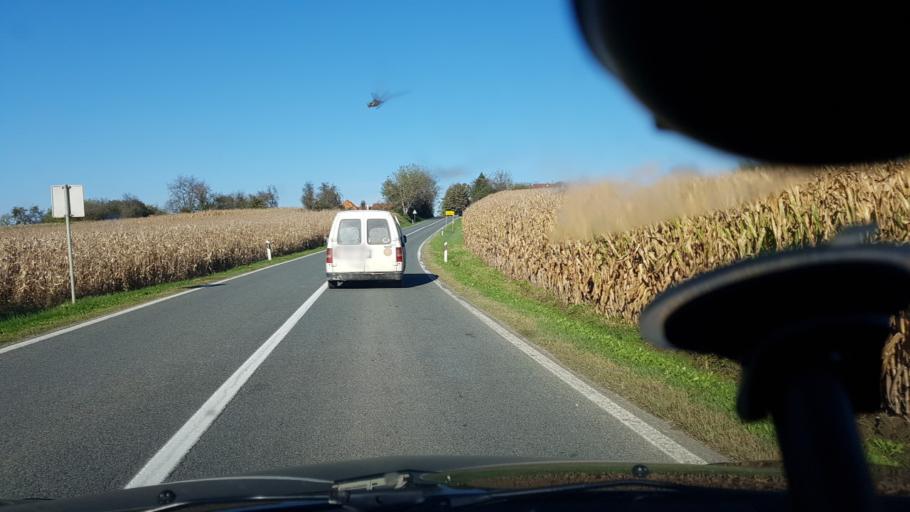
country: HR
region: Bjelovarsko-Bilogorska
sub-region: Grad Cazma
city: Cazma
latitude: 45.7941
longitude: 16.6956
